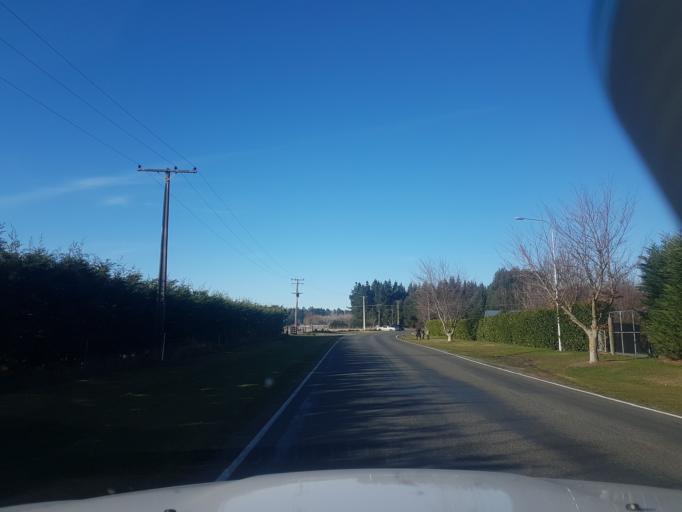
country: NZ
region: Canterbury
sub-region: Timaru District
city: Pleasant Point
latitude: -44.2562
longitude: 171.1295
